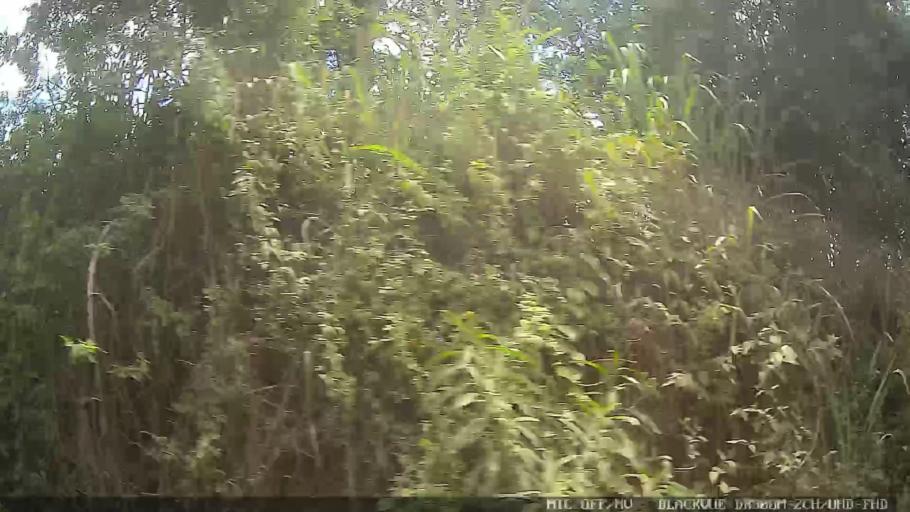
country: BR
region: Sao Paulo
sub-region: Atibaia
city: Atibaia
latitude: -23.1379
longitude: -46.6054
